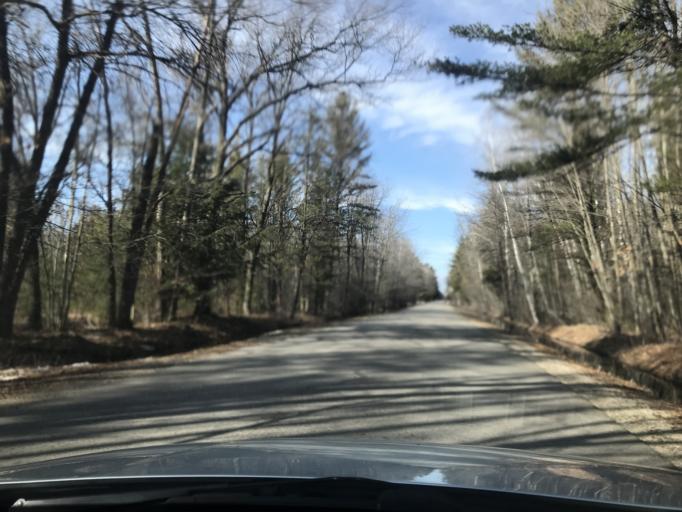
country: US
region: Wisconsin
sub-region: Marinette County
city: Marinette
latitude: 45.0257
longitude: -87.6674
